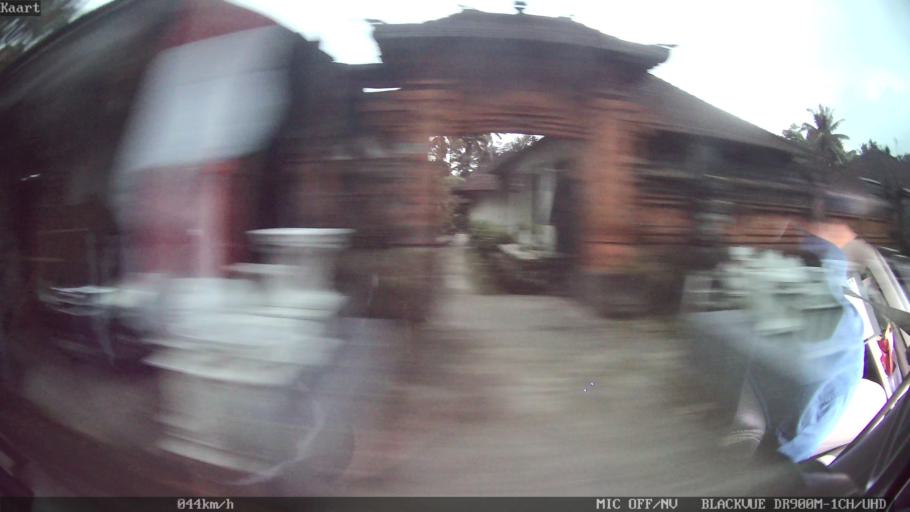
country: ID
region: Bali
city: Bayad
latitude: -8.4426
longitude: 115.2439
